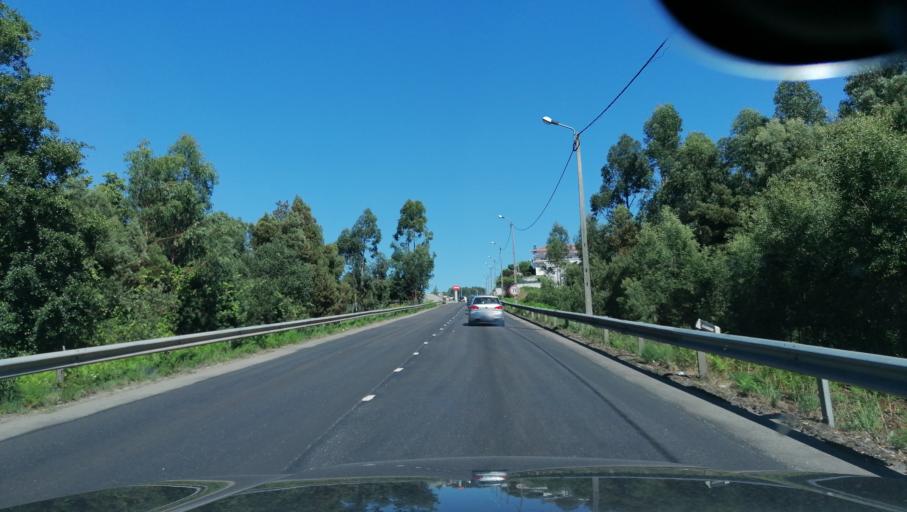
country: PT
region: Aveiro
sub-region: Santa Maria da Feira
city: Feira
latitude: 40.9314
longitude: -8.5309
